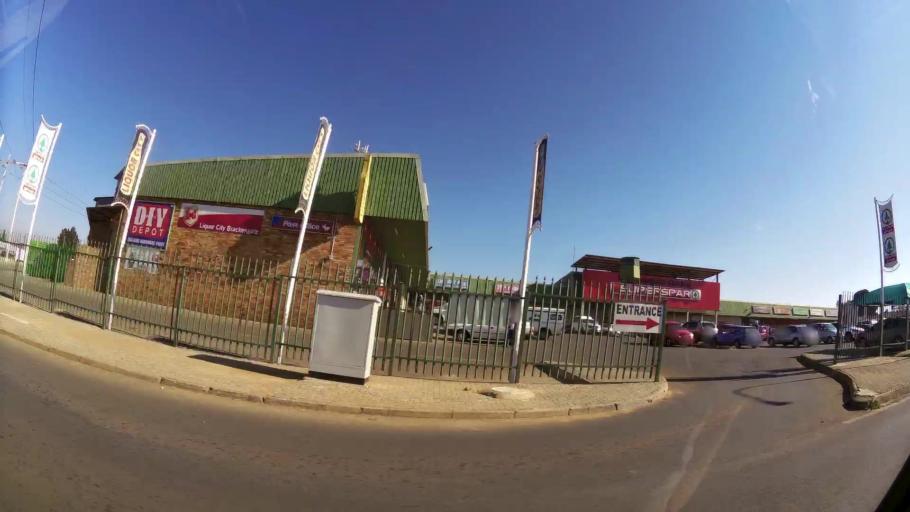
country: ZA
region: Gauteng
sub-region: Ekurhuleni Metropolitan Municipality
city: Germiston
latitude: -26.3398
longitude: 28.0959
